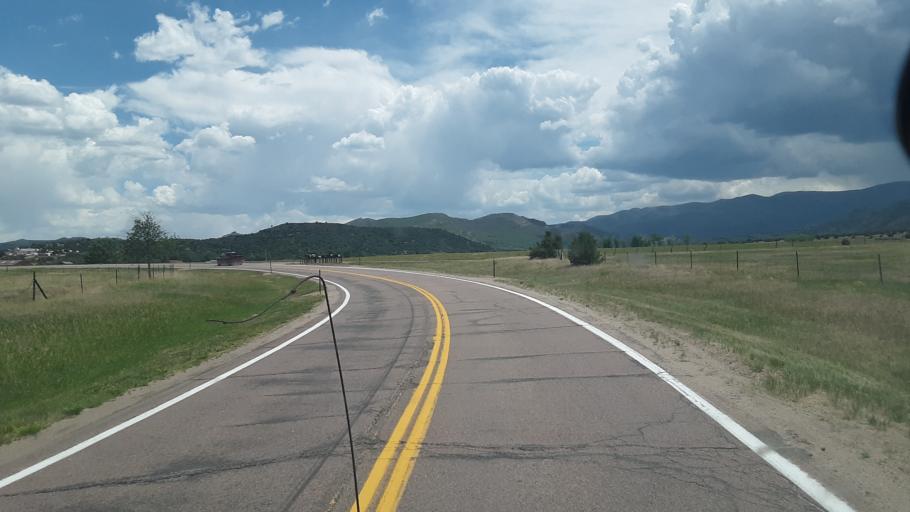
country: US
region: Colorado
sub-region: Fremont County
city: Florence
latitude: 38.2448
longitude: -105.0903
